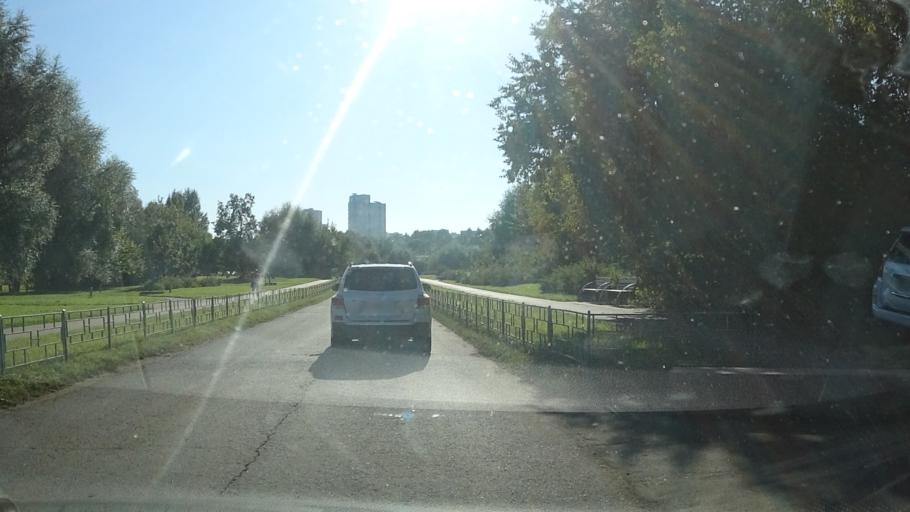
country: RU
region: Moscow
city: Shchukino
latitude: 55.7711
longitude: 37.4305
